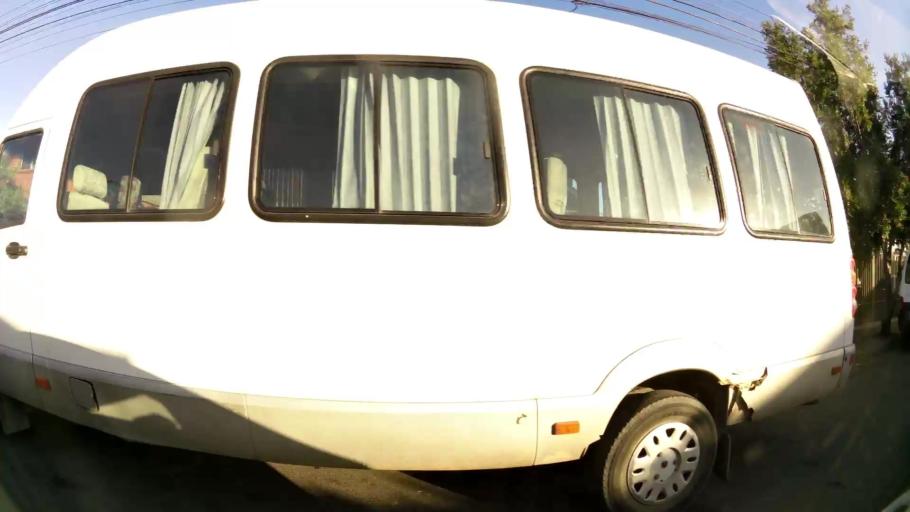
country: CL
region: Maule
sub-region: Provincia de Talca
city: Talca
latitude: -35.4444
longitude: -71.6746
